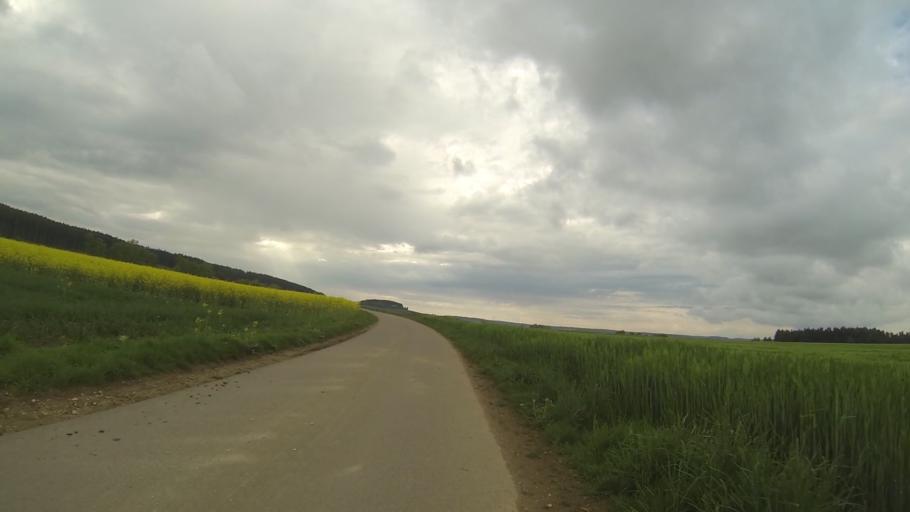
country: DE
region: Bavaria
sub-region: Swabia
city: Wittislingen
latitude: 48.6259
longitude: 10.3955
